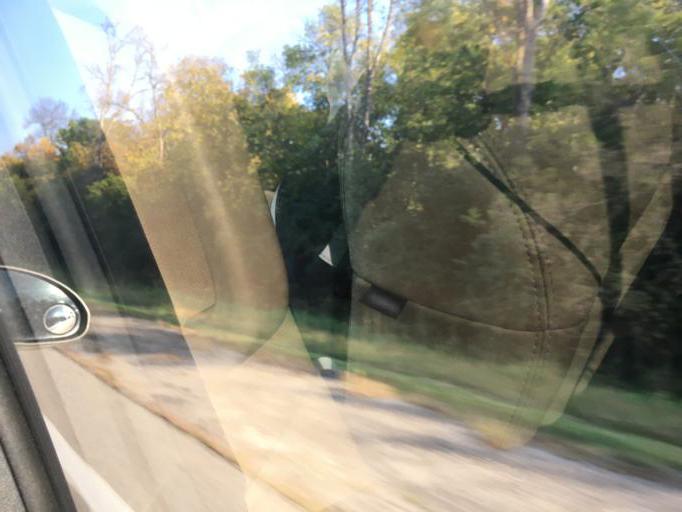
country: US
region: Minnesota
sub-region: Olmsted County
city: Rochester
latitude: 43.9926
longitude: -92.4028
